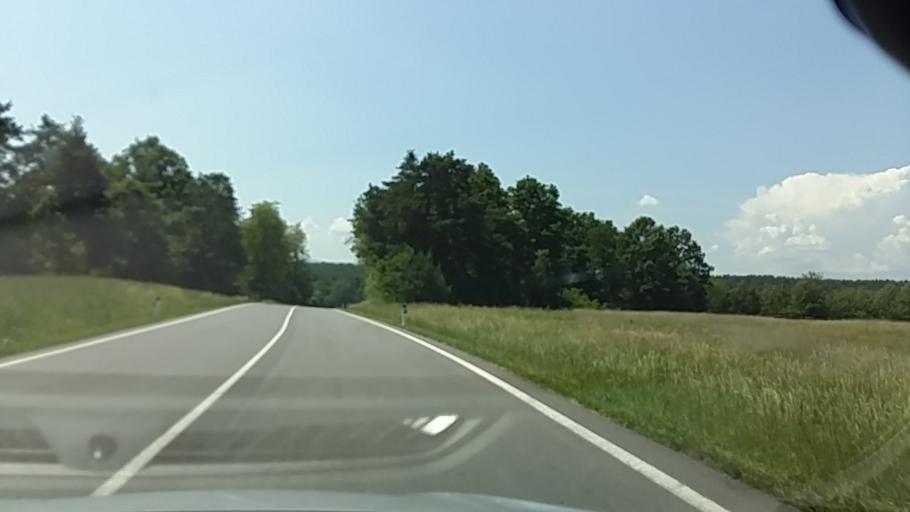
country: AT
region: Burgenland
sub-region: Politischer Bezirk Oberpullendorf
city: Oberpullendorf
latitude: 47.5252
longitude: 16.5121
